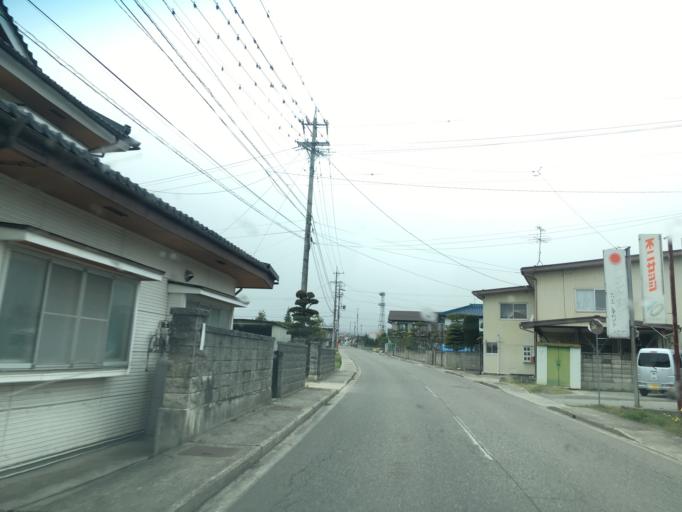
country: JP
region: Nagano
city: Omachi
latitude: 36.5111
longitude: 137.8478
